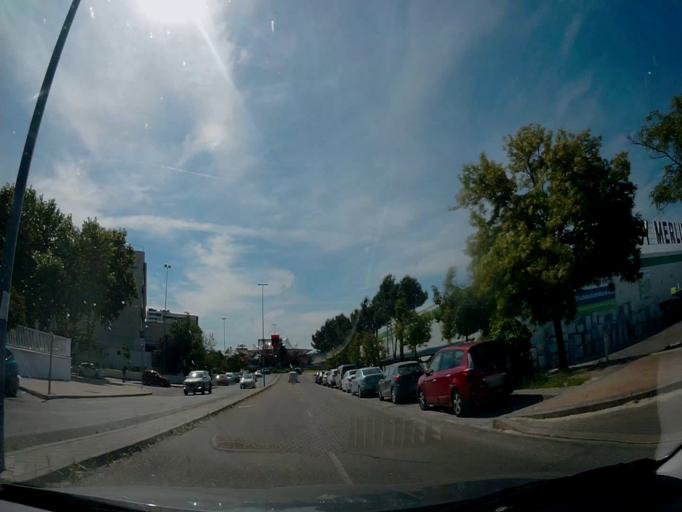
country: ES
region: Madrid
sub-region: Provincia de Madrid
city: Mostoles
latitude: 40.3431
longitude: -3.8502
